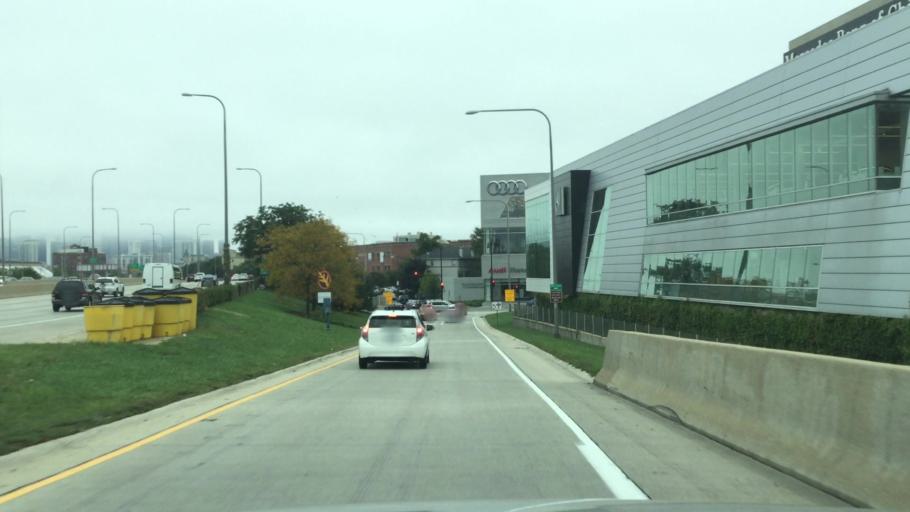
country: US
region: Illinois
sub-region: Cook County
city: Chicago
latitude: 41.9119
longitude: -87.6663
